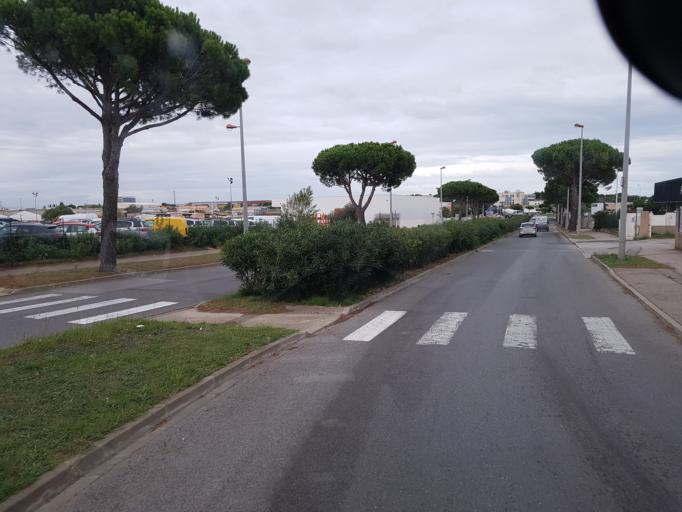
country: FR
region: Languedoc-Roussillon
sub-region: Departement de l'Aude
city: Narbonne
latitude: 43.1576
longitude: 2.9786
